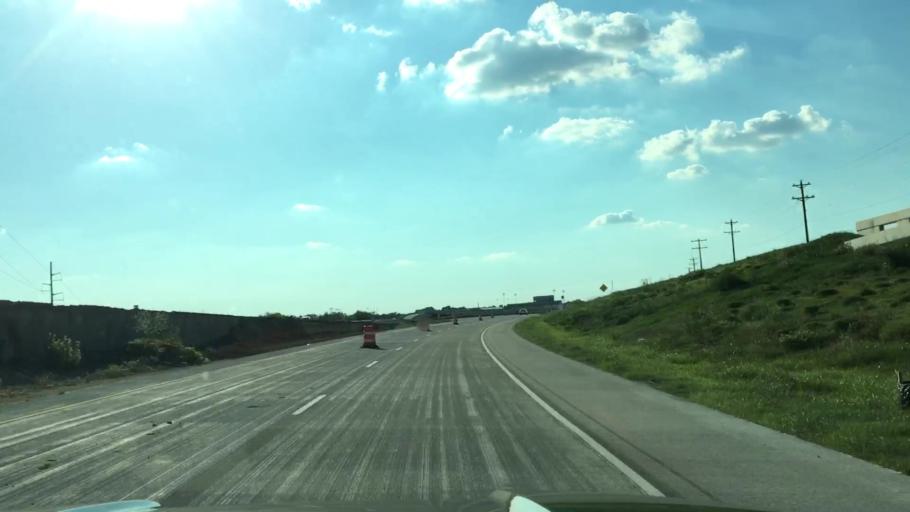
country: US
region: Texas
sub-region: Denton County
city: Justin
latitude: 33.0270
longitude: -97.3025
